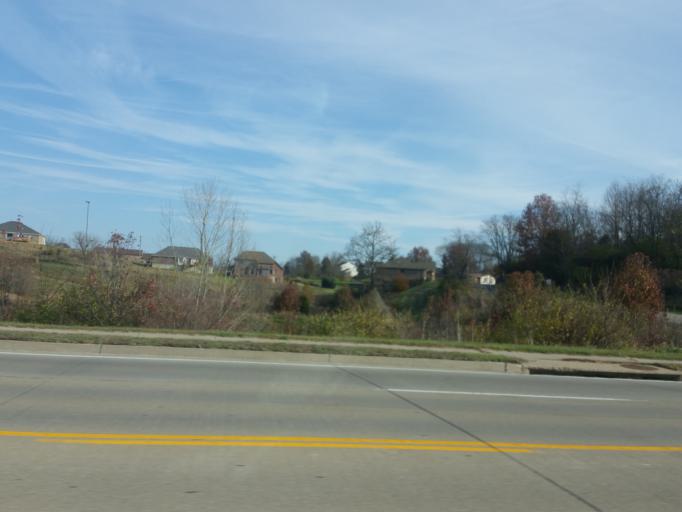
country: US
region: Kentucky
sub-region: Campbell County
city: Alexandria
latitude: 38.9456
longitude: -84.3939
